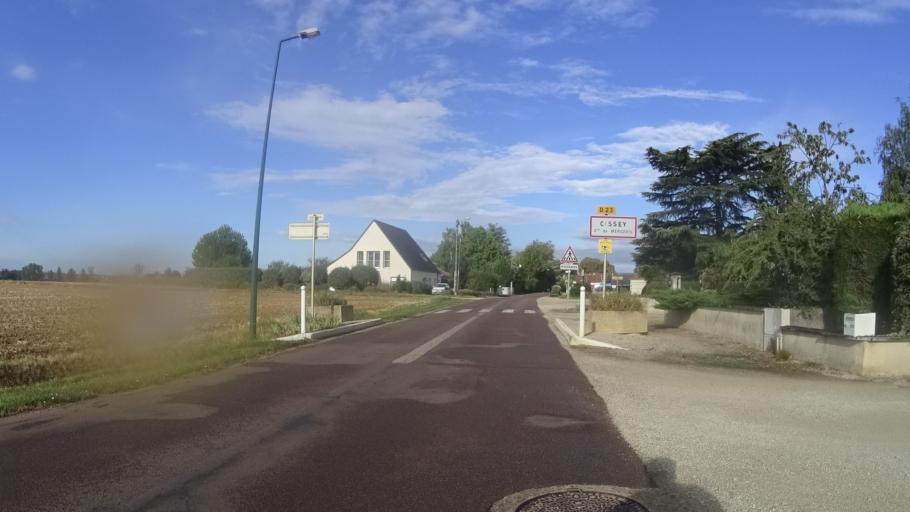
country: FR
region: Bourgogne
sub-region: Departement de Saone-et-Loire
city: Demigny
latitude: 46.9594
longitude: 4.8698
